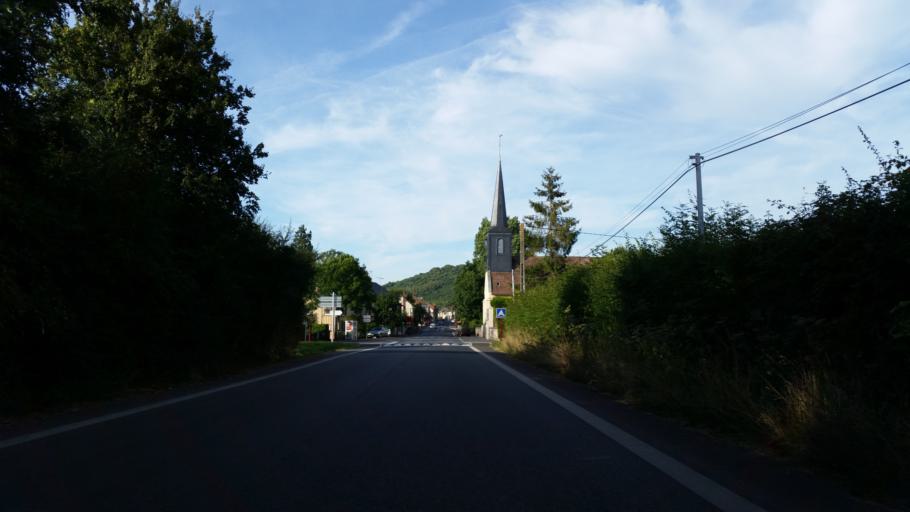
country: FR
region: Lower Normandy
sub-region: Departement du Calvados
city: Cambremer
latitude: 49.1140
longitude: 0.0109
